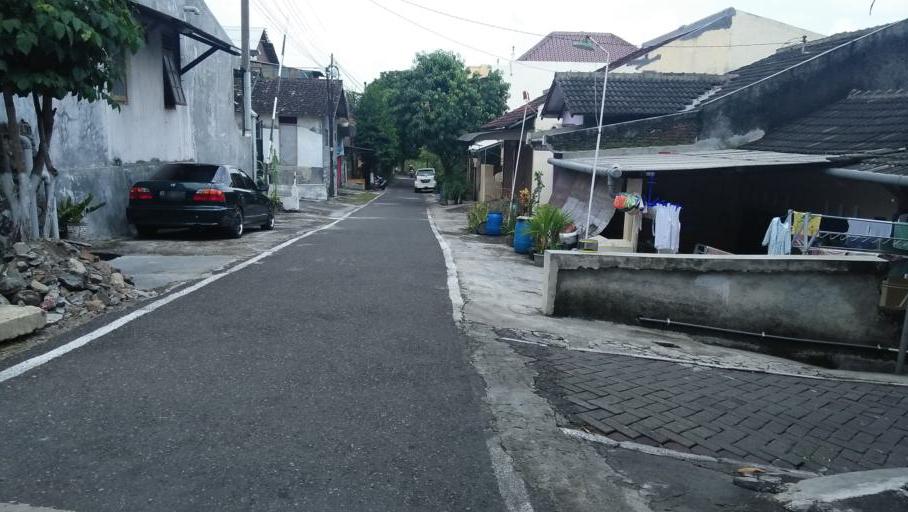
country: ID
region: Central Java
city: Semarang
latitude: -7.0362
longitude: 110.4511
